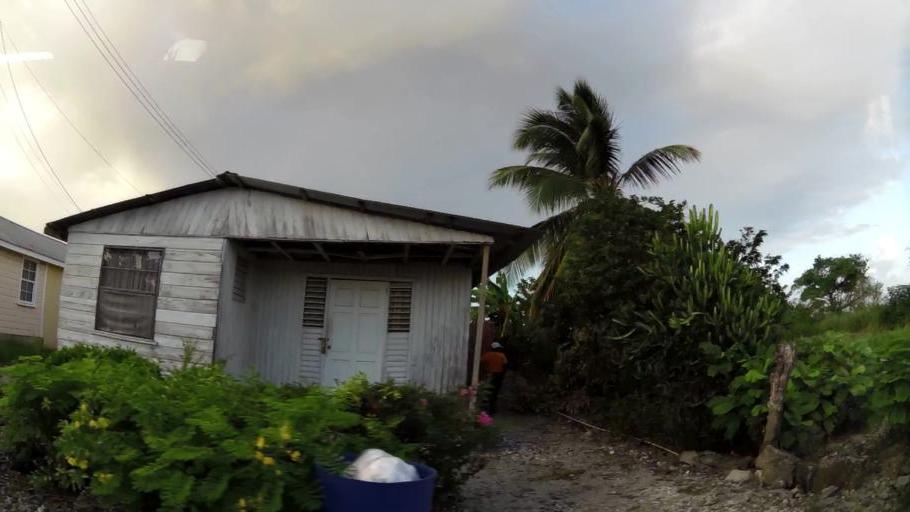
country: BB
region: Saint Philip
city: Crane
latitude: 13.1068
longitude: -59.4686
